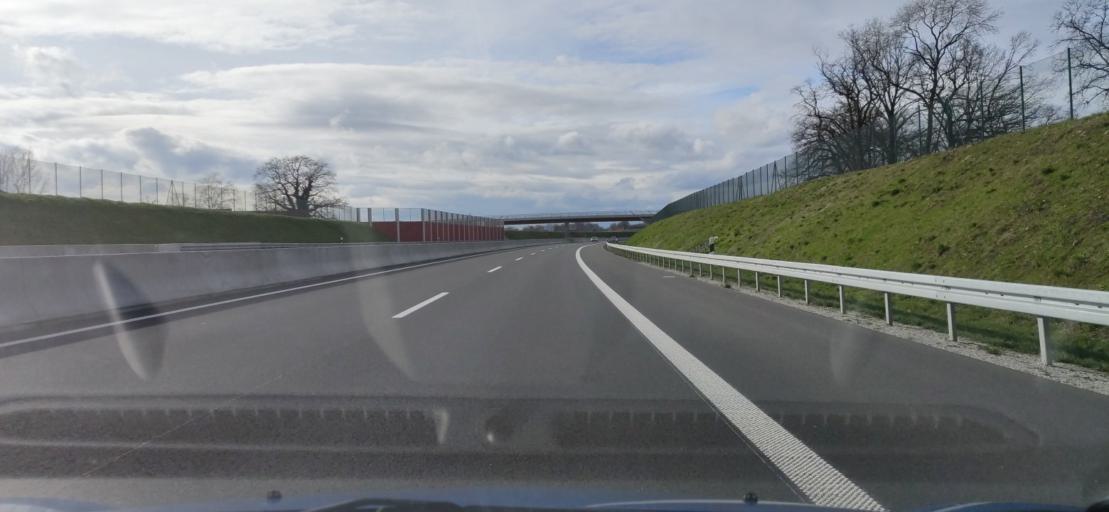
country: DE
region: North Rhine-Westphalia
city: Borgholzhausen
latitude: 52.0676
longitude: 8.2720
